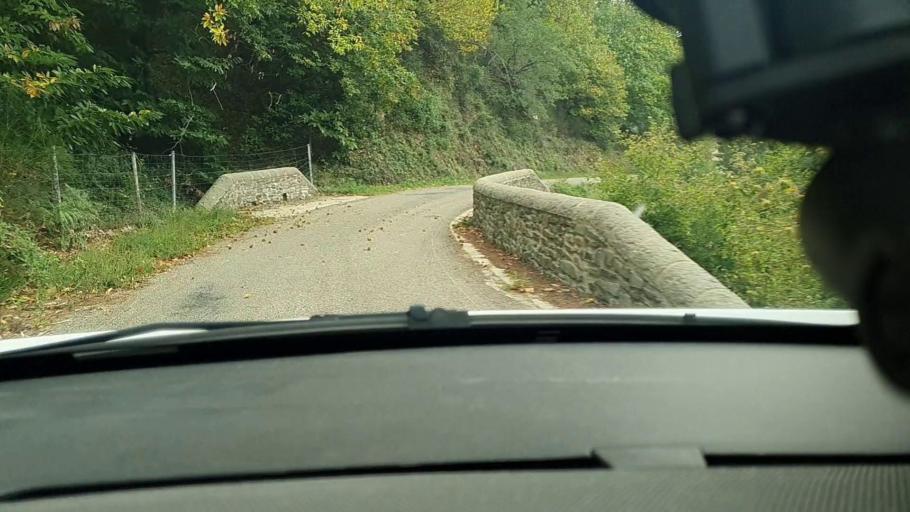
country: FR
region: Languedoc-Roussillon
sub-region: Departement du Gard
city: Branoux-les-Taillades
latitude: 44.2696
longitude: 3.9723
